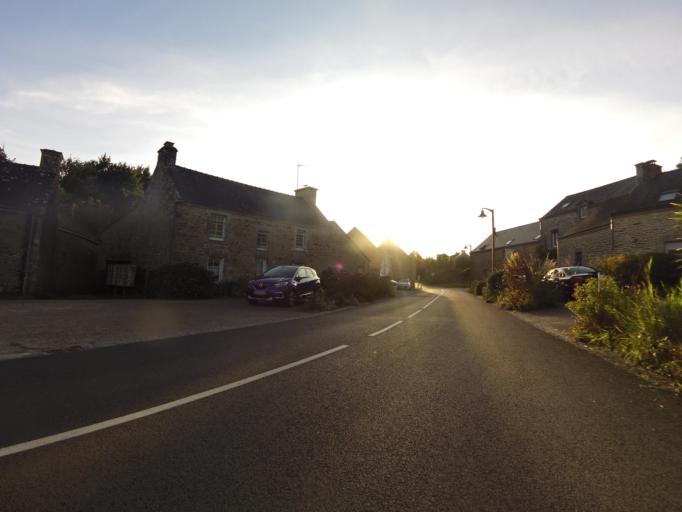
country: FR
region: Brittany
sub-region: Departement du Morbihan
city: Sulniac
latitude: 47.6402
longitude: -2.5990
